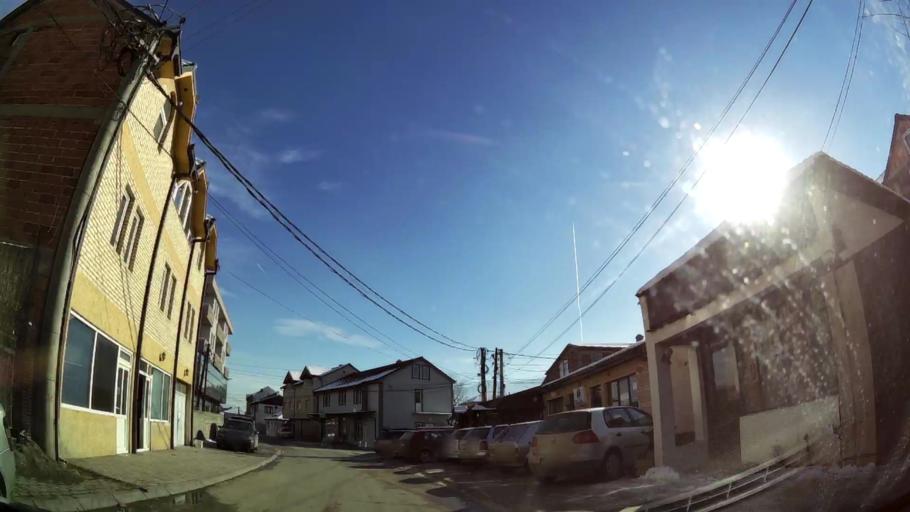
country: MK
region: Saraj
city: Saraj
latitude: 42.0007
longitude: 21.3210
